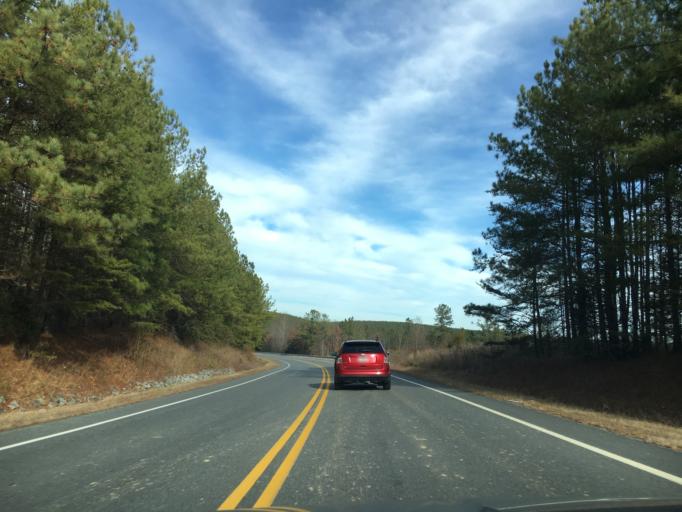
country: US
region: Virginia
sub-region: Louisa County
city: Louisa
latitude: 38.0612
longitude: -77.8797
